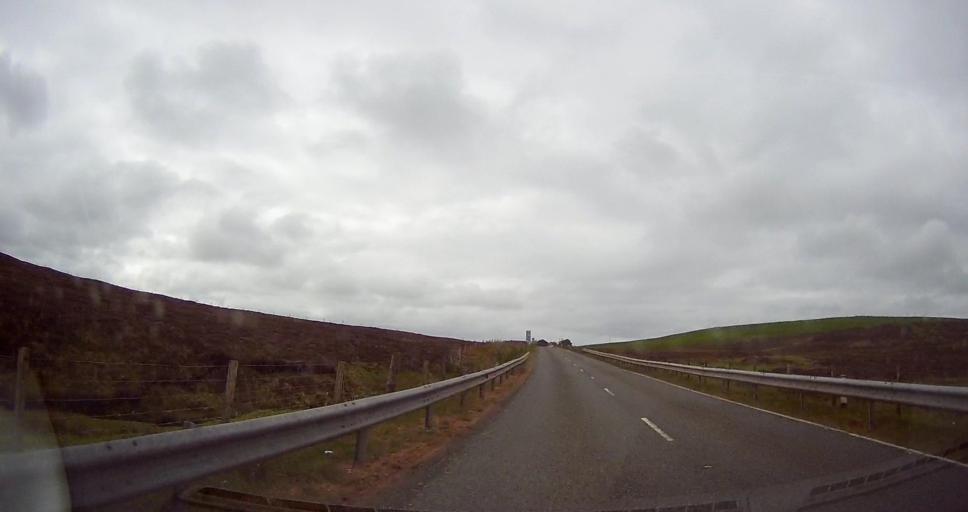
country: GB
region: Scotland
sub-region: Shetland Islands
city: Lerwick
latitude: 60.2522
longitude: -1.3887
